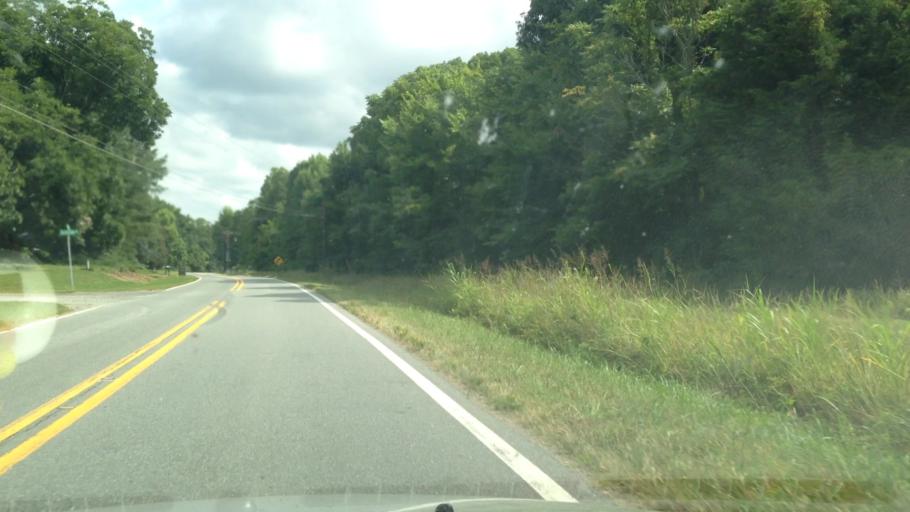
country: US
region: North Carolina
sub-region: Rockingham County
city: Reidsville
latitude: 36.4283
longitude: -79.5814
